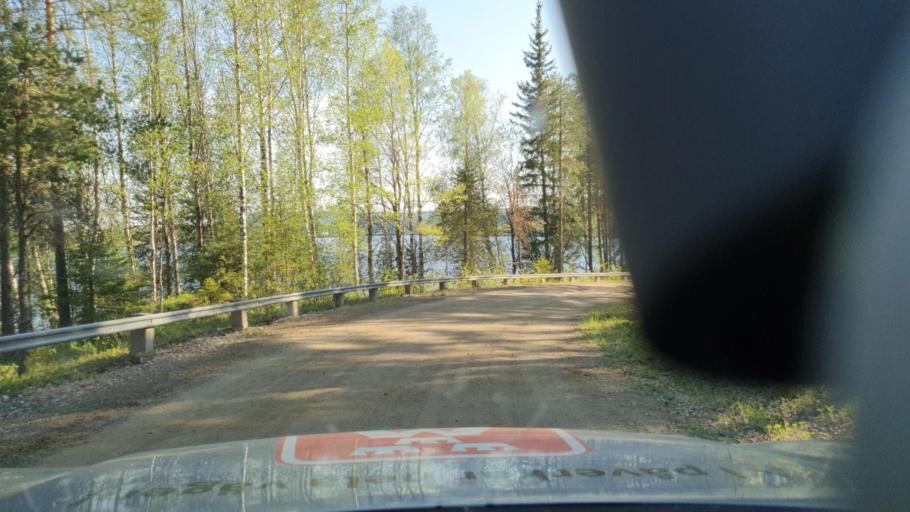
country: SE
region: Norrbotten
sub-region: Alvsbyns Kommun
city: AElvsbyn
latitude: 66.2306
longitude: 20.8650
